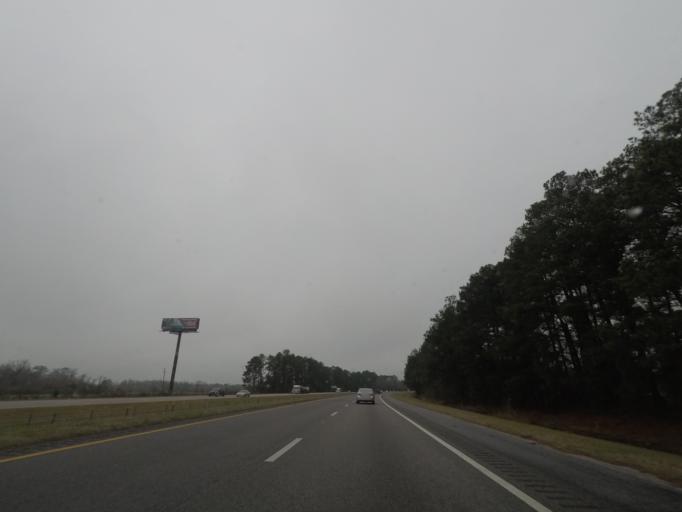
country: US
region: South Carolina
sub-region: Florence County
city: Timmonsville
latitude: 33.9624
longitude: -80.0449
